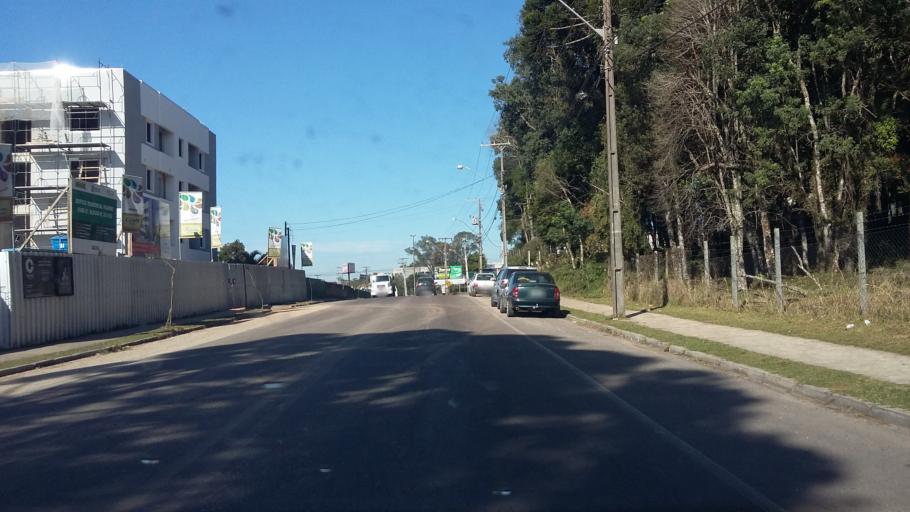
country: BR
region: Parana
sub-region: Campo Largo
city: Campo Largo
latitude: -25.4548
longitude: -49.5416
